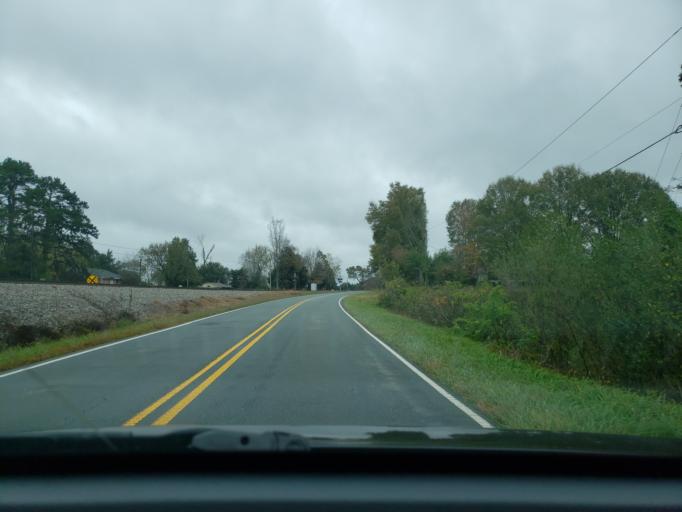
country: US
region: North Carolina
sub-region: Stokes County
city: Walnut Cove
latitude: 36.2393
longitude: -80.1548
